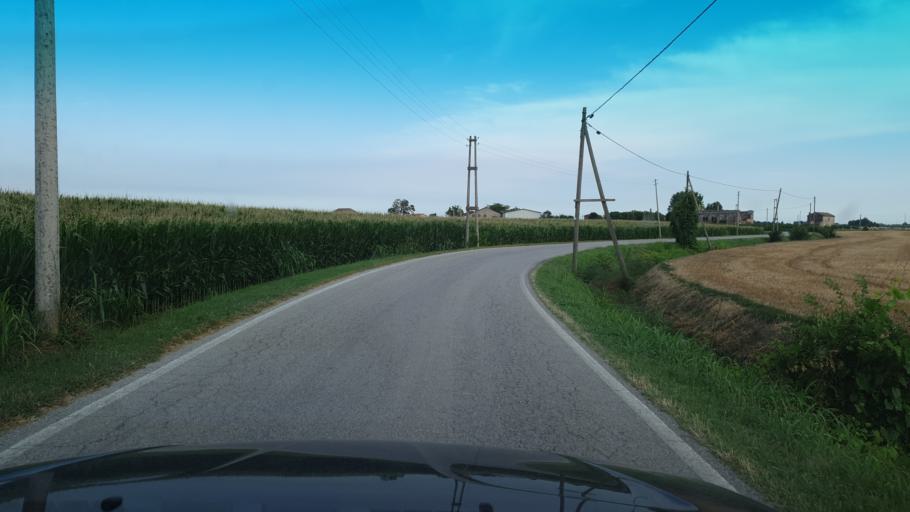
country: IT
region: Veneto
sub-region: Provincia di Rovigo
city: Castelguglielmo
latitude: 45.0052
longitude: 11.5286
